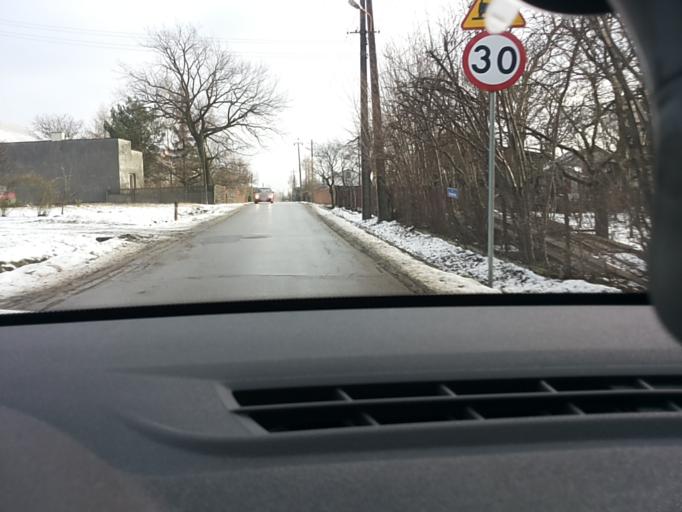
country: PL
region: Lodz Voivodeship
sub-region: Skierniewice
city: Skierniewice
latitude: 51.9711
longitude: 20.1152
